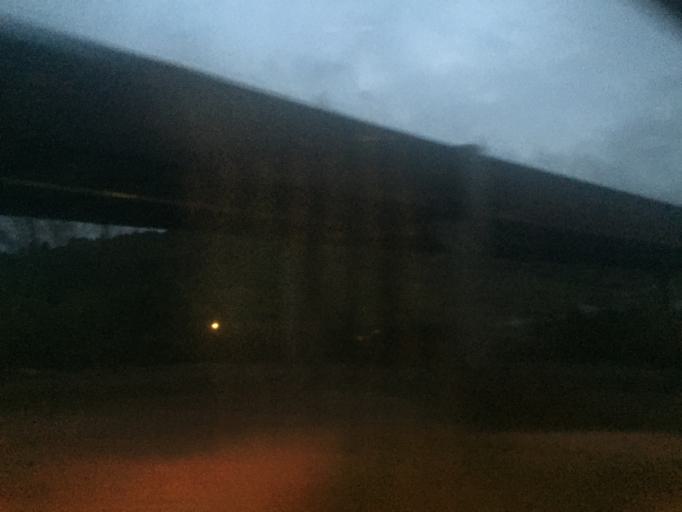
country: IT
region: The Marches
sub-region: Provincia di Macerata
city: Muccia
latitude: 43.0768
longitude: 13.0566
